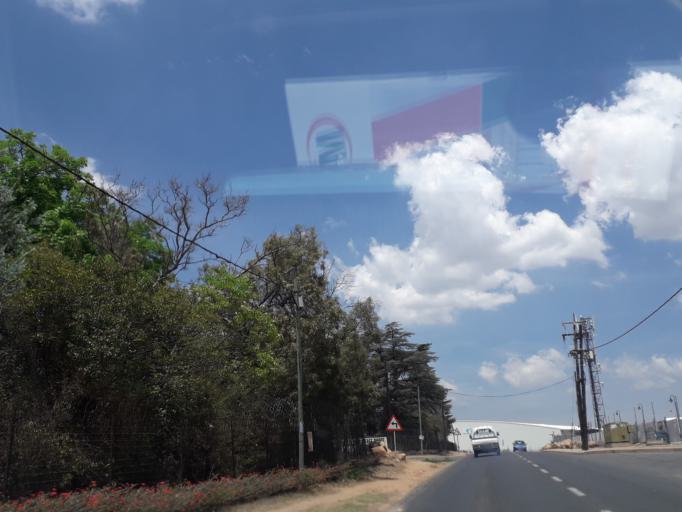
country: ZA
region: Gauteng
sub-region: West Rand District Municipality
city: Muldersdriseloop
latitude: -26.0703
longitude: 27.9234
